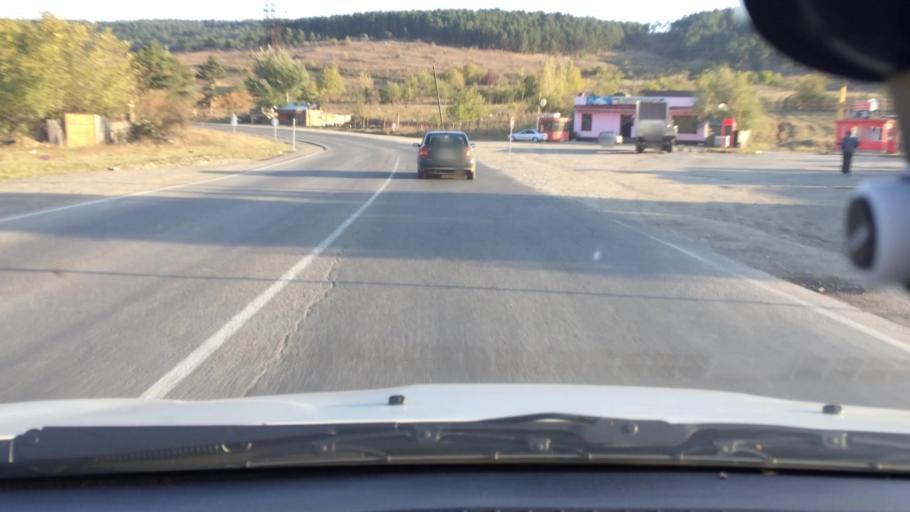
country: GE
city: Surami
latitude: 42.0105
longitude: 43.5779
